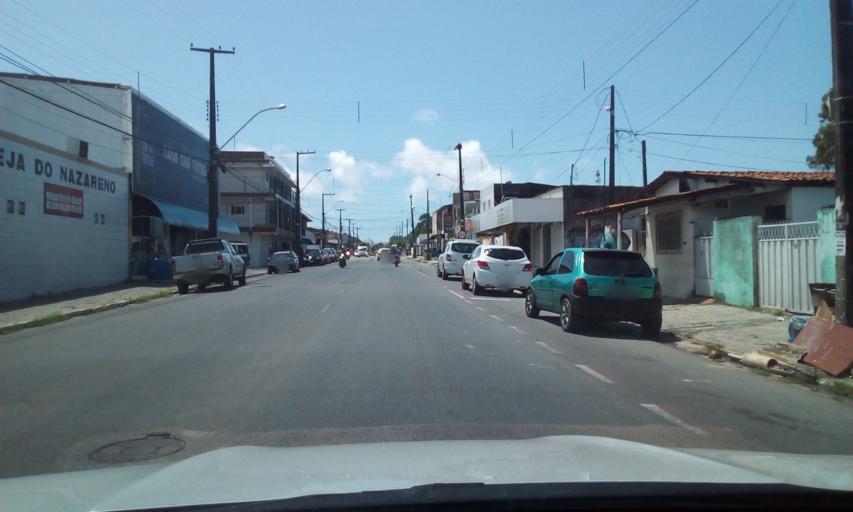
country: BR
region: Paraiba
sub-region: Joao Pessoa
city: Joao Pessoa
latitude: -7.1697
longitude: -34.8343
